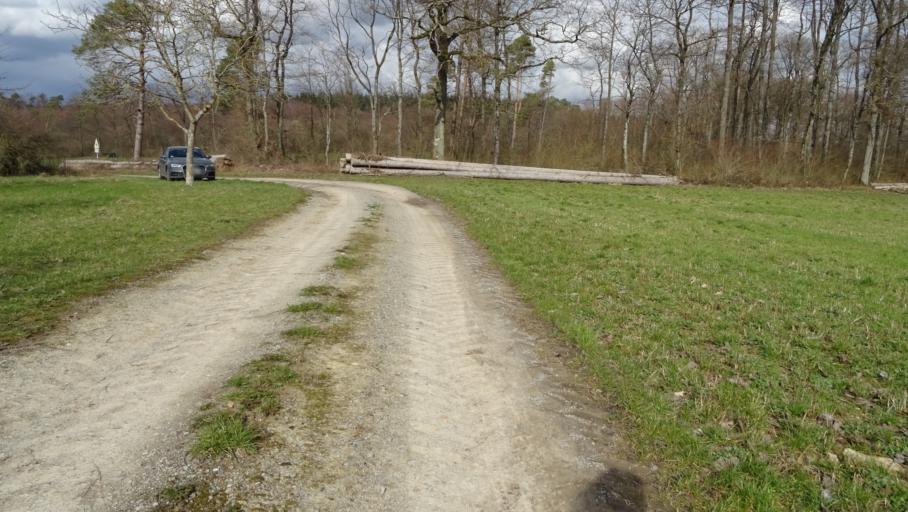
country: DE
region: Baden-Wuerttemberg
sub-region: Karlsruhe Region
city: Limbach
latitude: 49.4346
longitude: 9.2612
